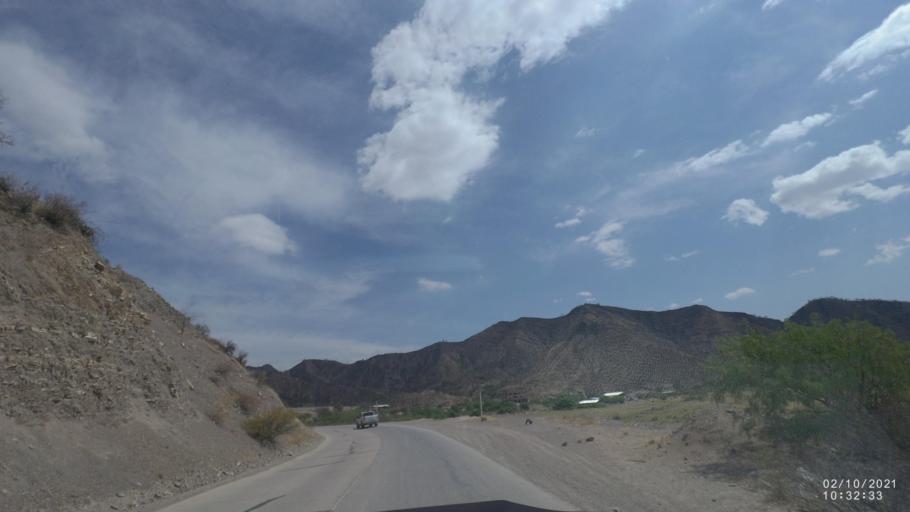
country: BO
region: Cochabamba
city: Capinota
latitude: -17.6872
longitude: -66.2586
